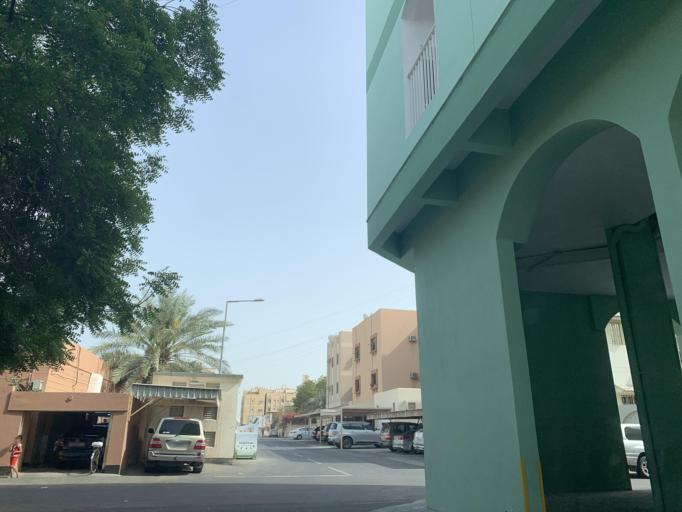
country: BH
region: Northern
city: Ar Rifa'
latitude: 26.1248
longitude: 50.5734
